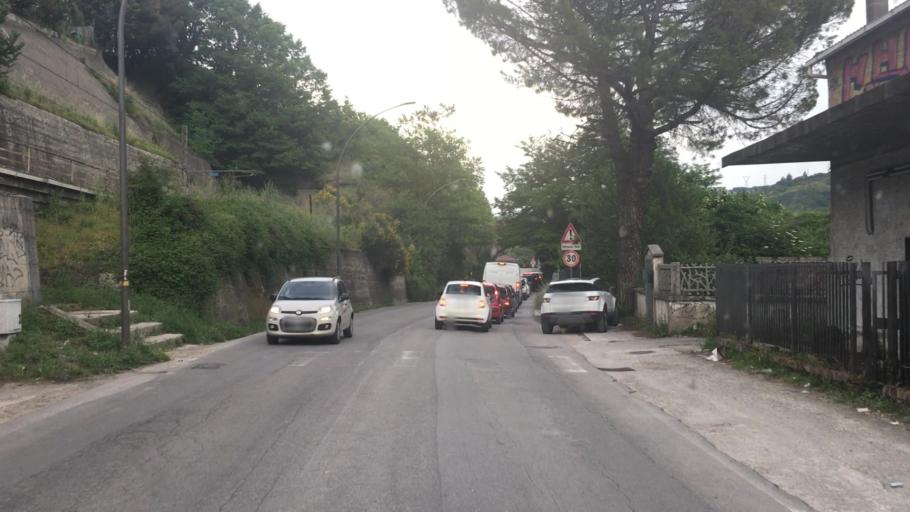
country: IT
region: Basilicate
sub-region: Provincia di Potenza
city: Potenza
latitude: 40.6248
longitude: 15.7900
